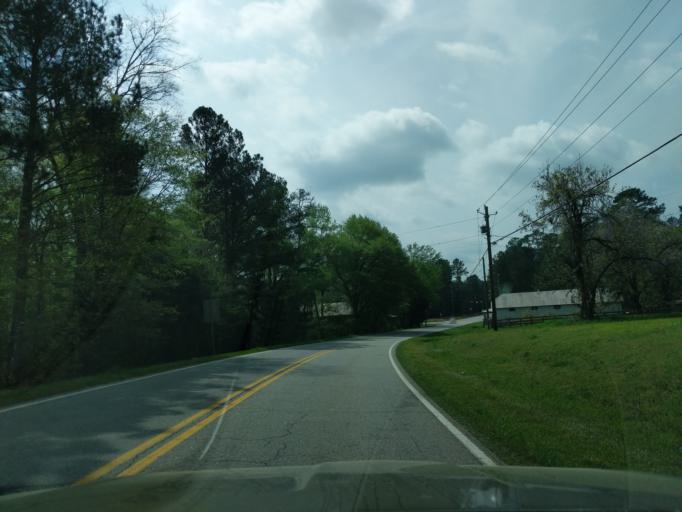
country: US
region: Georgia
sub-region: Columbia County
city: Appling
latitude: 33.5580
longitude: -82.3186
